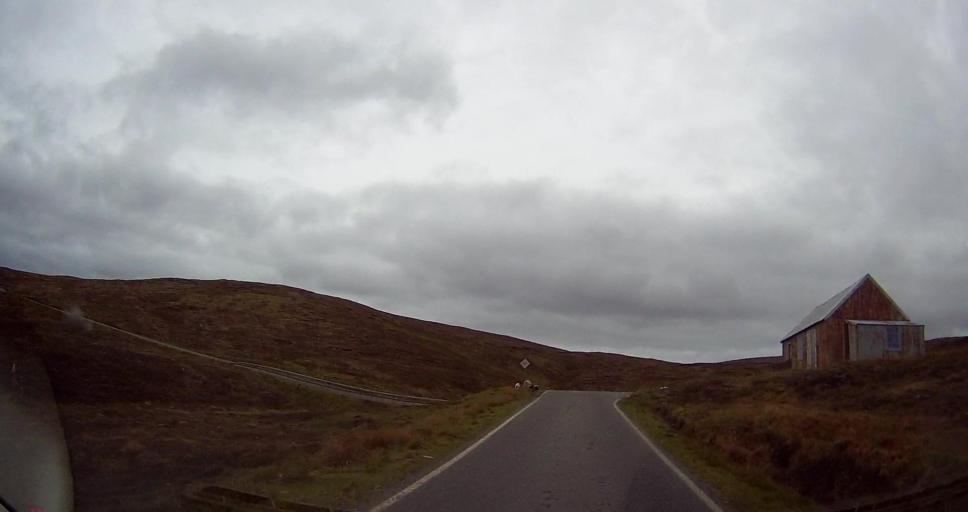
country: GB
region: Scotland
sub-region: Shetland Islands
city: Shetland
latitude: 60.5500
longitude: -1.0615
